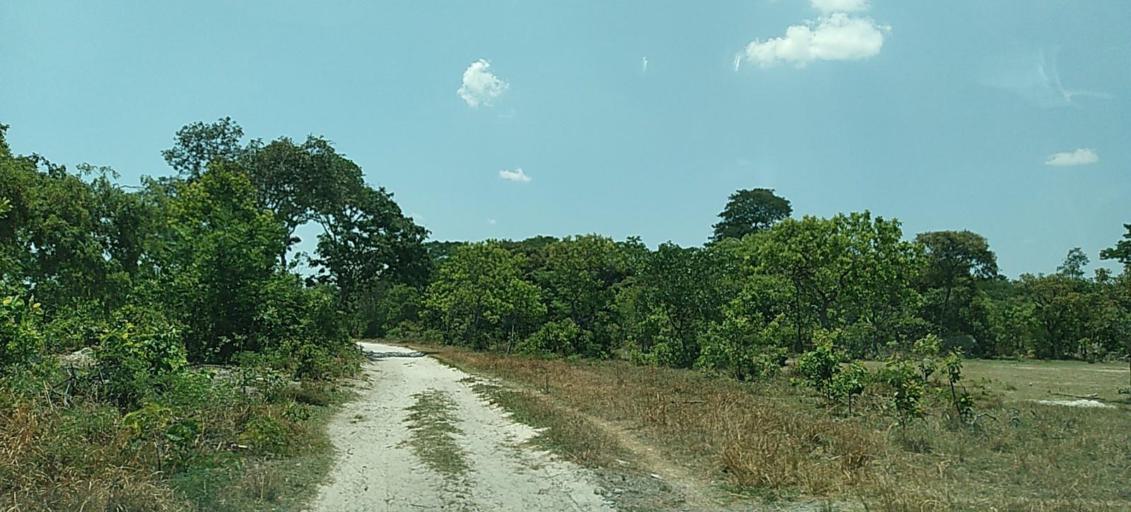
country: ZM
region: Central
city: Kapiri Mposhi
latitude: -13.6710
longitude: 28.5011
